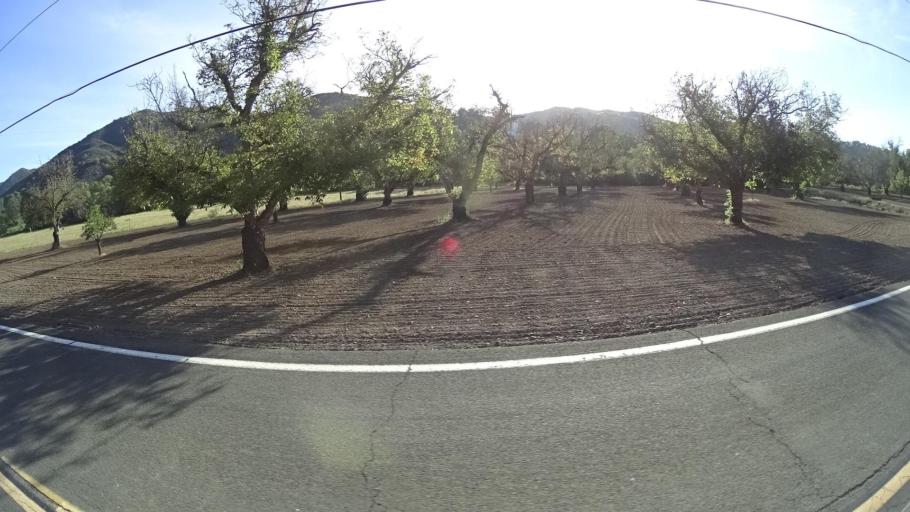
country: US
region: California
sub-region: Lake County
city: Upper Lake
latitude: 39.1248
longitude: -122.9946
